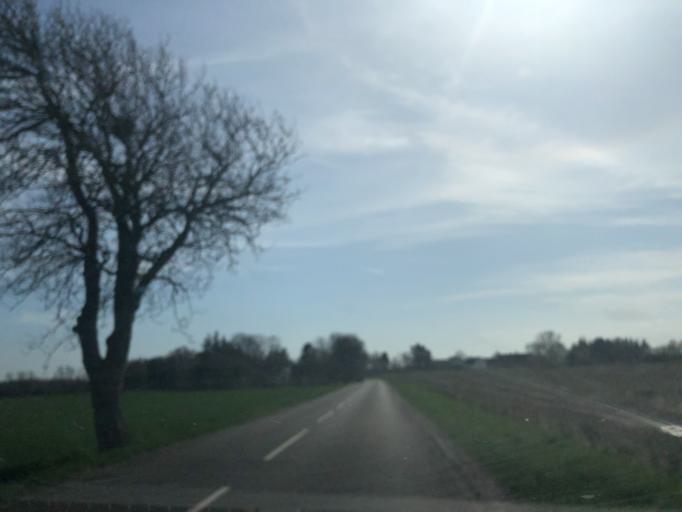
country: DK
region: Zealand
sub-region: Faxe Kommune
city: Ronnede
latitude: 55.2940
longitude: 12.0700
